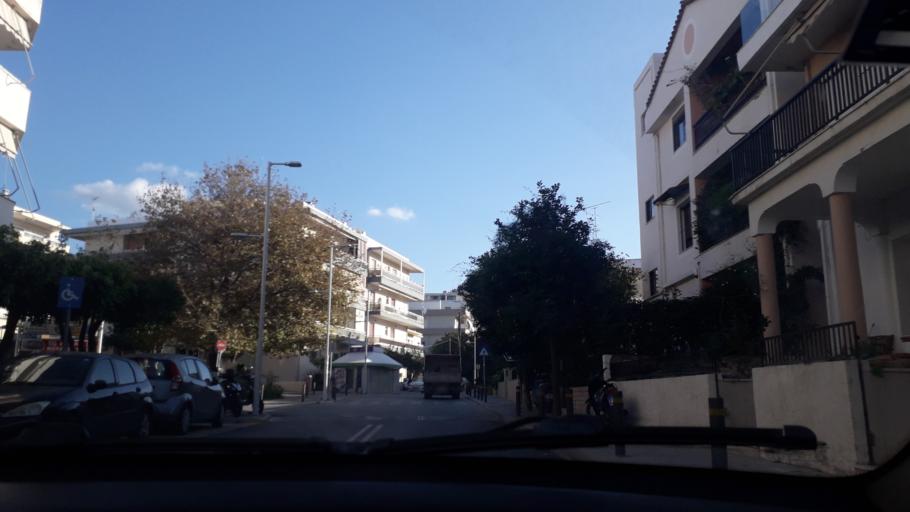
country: GR
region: Crete
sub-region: Nomos Rethymnis
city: Rethymno
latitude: 35.3635
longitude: 24.4718
